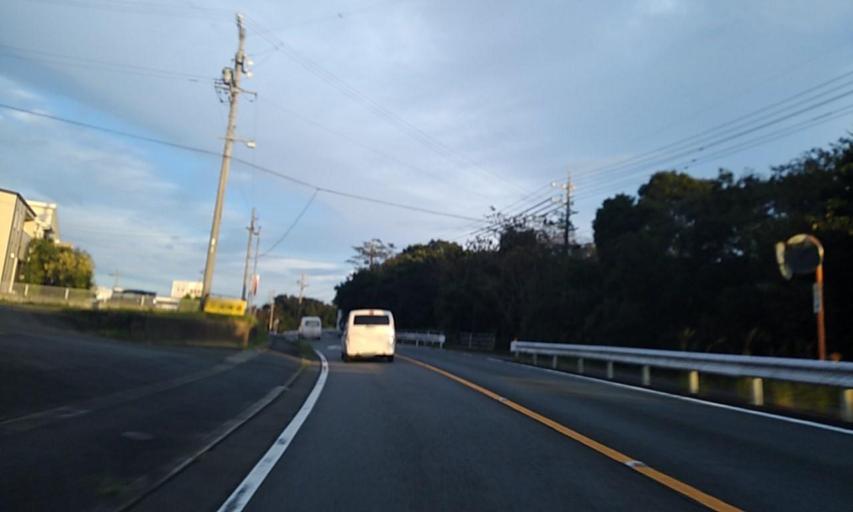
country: JP
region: Mie
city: Toba
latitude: 34.3241
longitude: 136.8429
